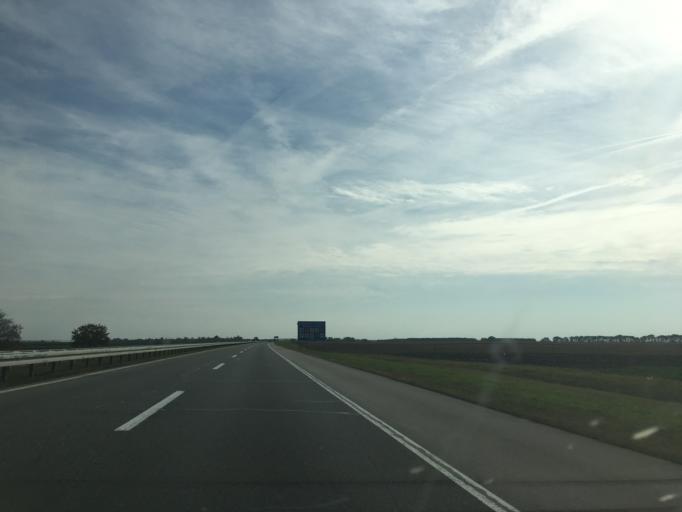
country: RS
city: Novi Karlovci
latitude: 45.0410
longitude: 20.1811
